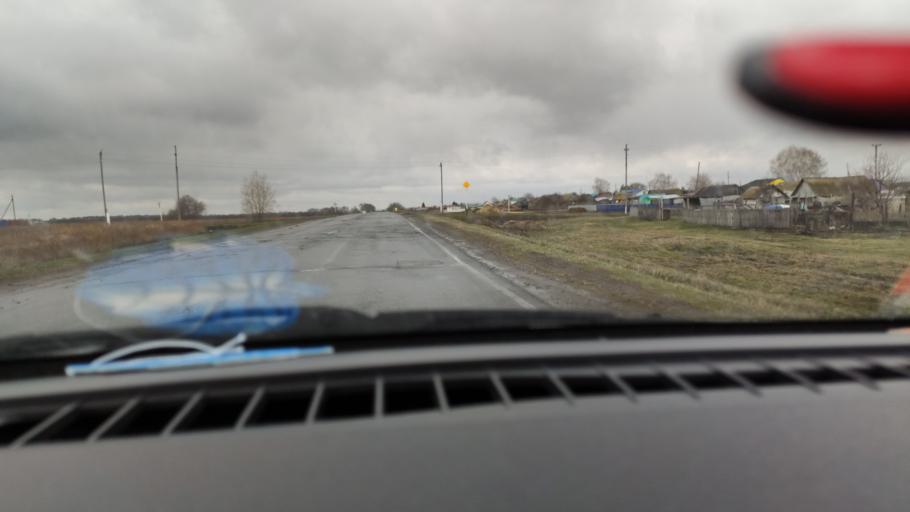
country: RU
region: Samara
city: Koshki
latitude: 54.1654
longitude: 50.4821
